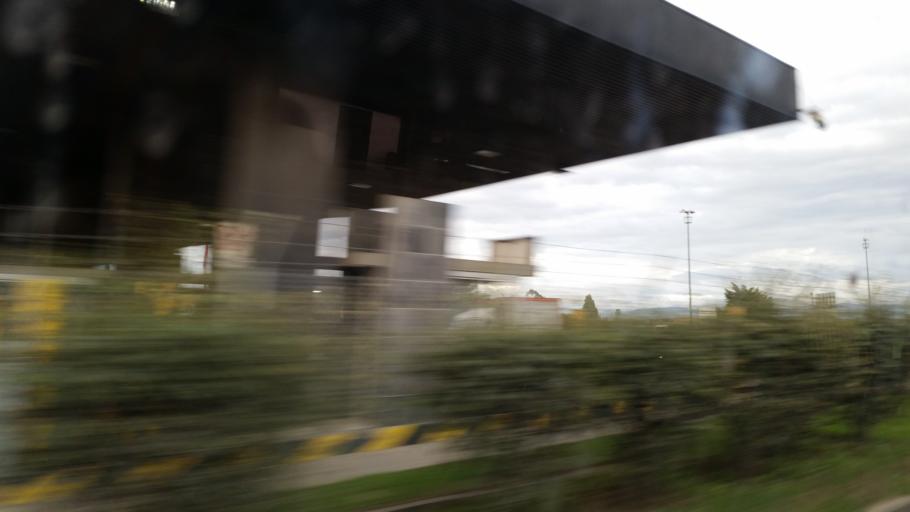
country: CO
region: Cundinamarca
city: Funza
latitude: 4.6983
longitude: -74.1794
